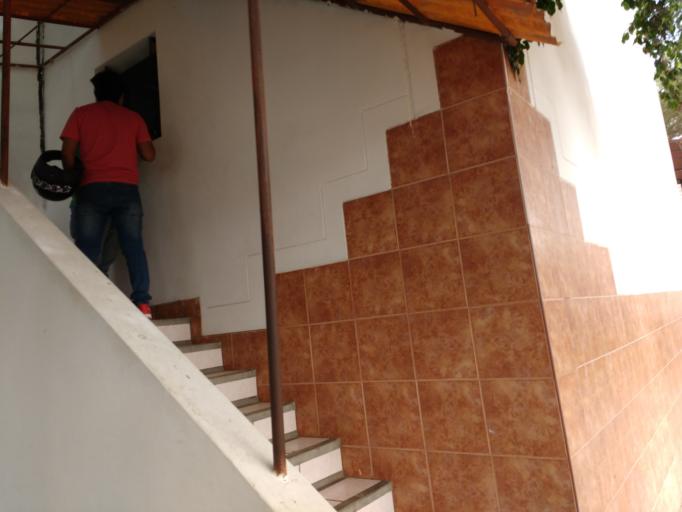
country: PE
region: Piura
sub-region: Provincia de Piura
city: Piura
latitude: -5.1824
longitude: -80.6189
